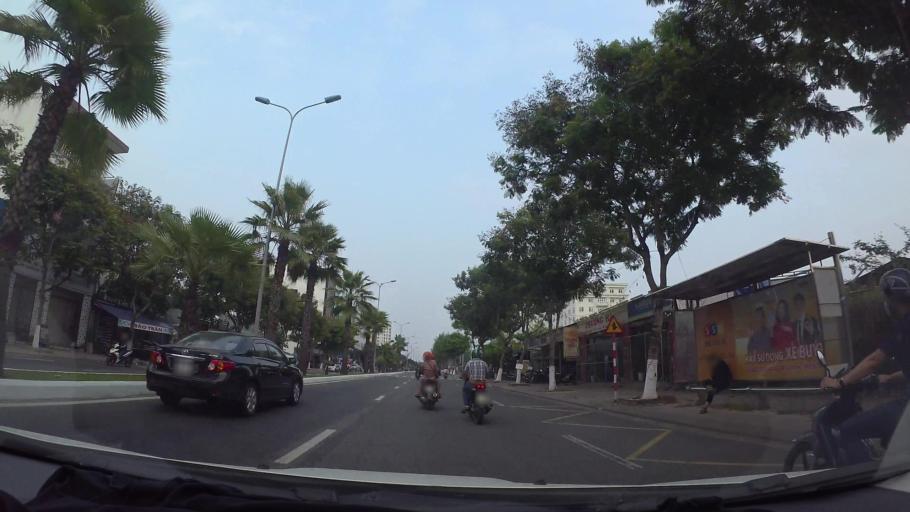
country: VN
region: Da Nang
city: Cam Le
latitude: 16.0324
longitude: 108.2196
